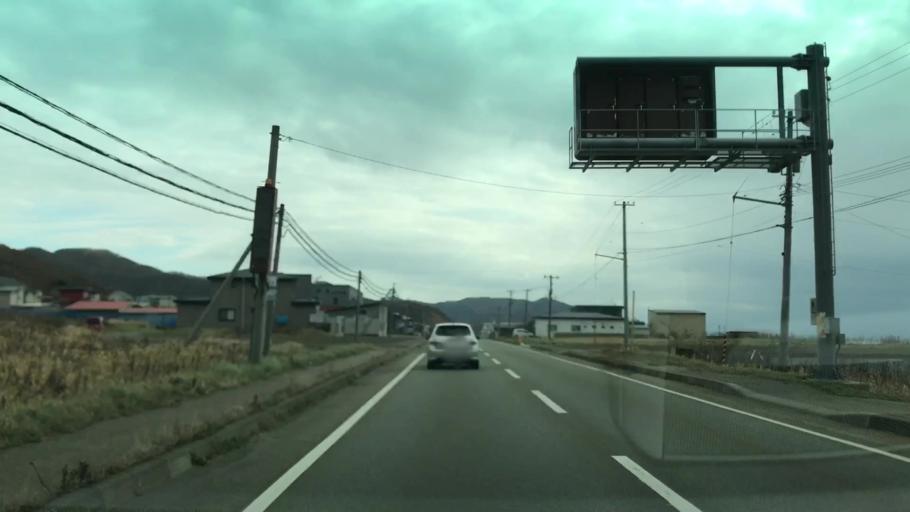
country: JP
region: Hokkaido
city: Shizunai-furukawacho
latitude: 42.0270
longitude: 143.1371
